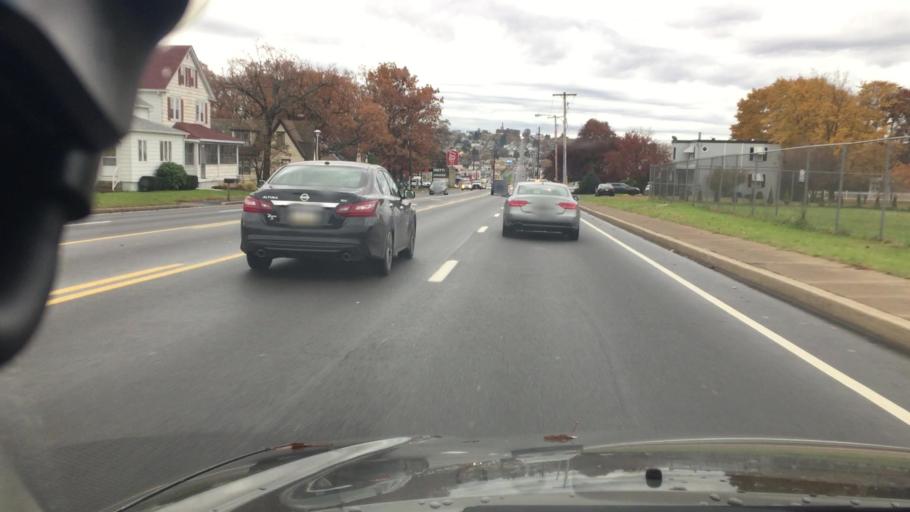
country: US
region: Pennsylvania
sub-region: Luzerne County
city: Harleigh
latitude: 40.9859
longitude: -75.9817
